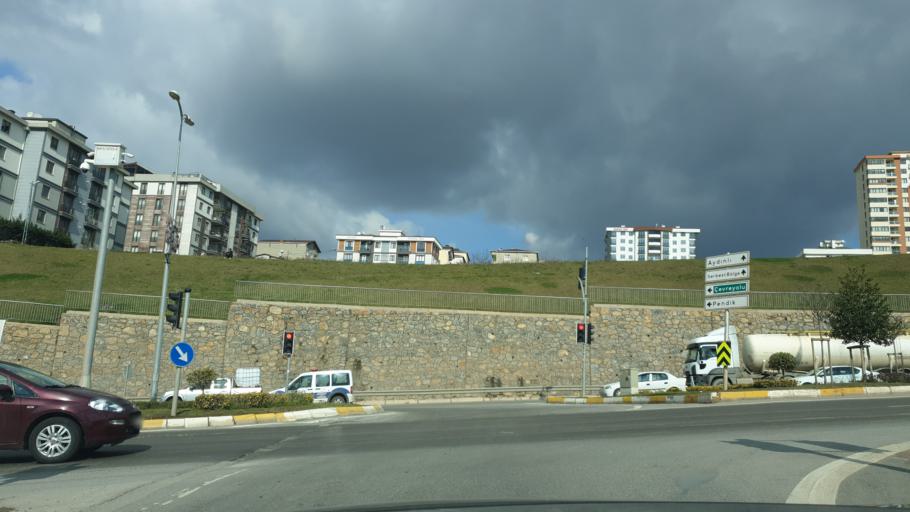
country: TR
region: Istanbul
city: Icmeler
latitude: 40.8759
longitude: 29.3199
